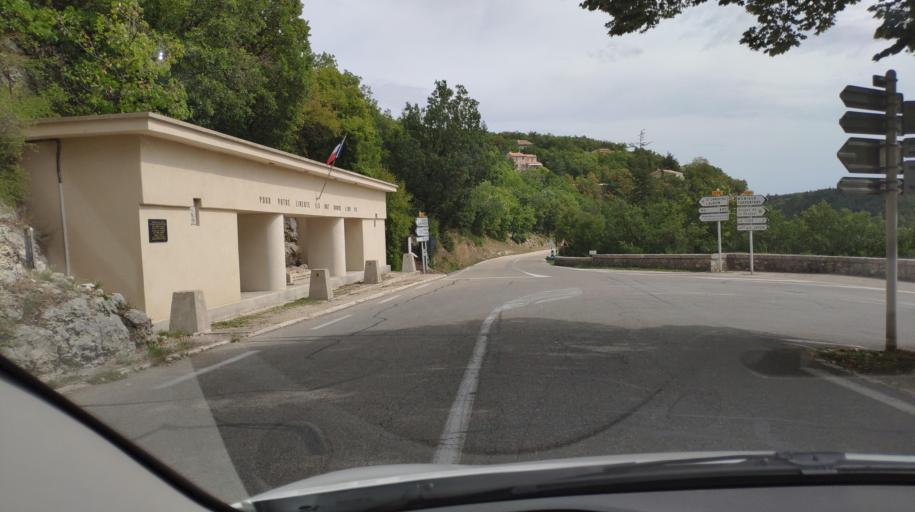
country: FR
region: Provence-Alpes-Cote d'Azur
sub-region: Departement du Vaucluse
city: Sault
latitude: 44.0886
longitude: 5.4128
